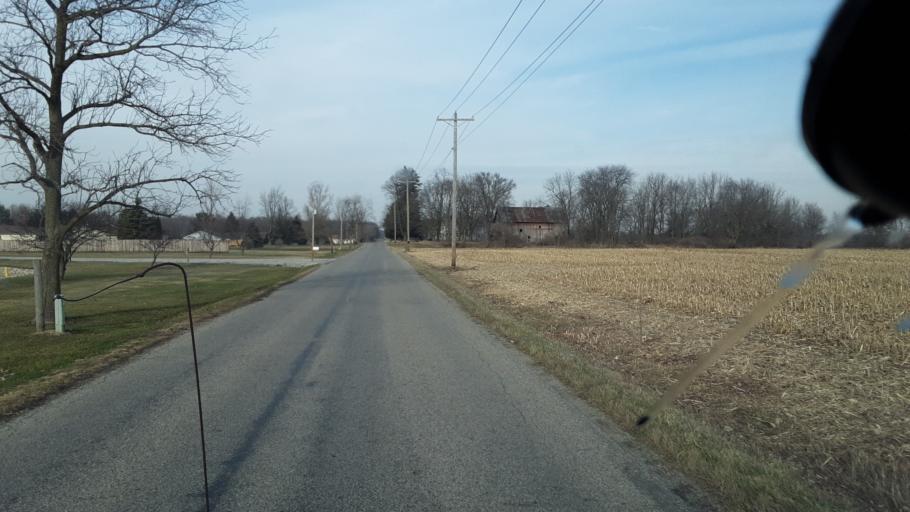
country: US
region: Indiana
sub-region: DeKalb County
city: Butler
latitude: 41.4035
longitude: -84.8893
